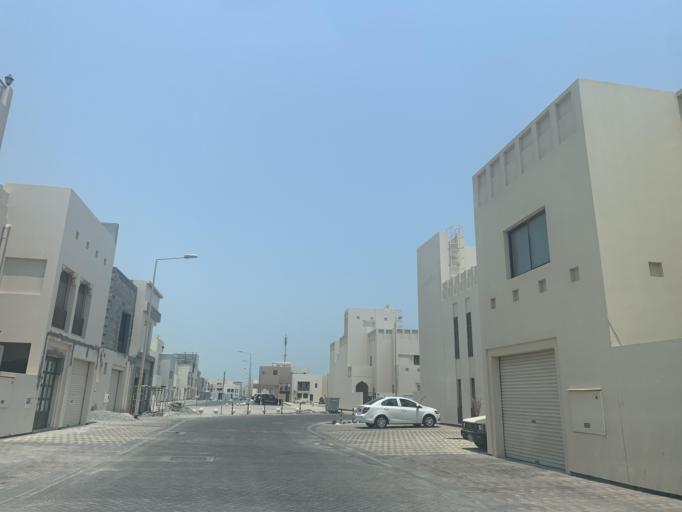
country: BH
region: Muharraq
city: Al Hadd
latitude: 26.2318
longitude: 50.6764
